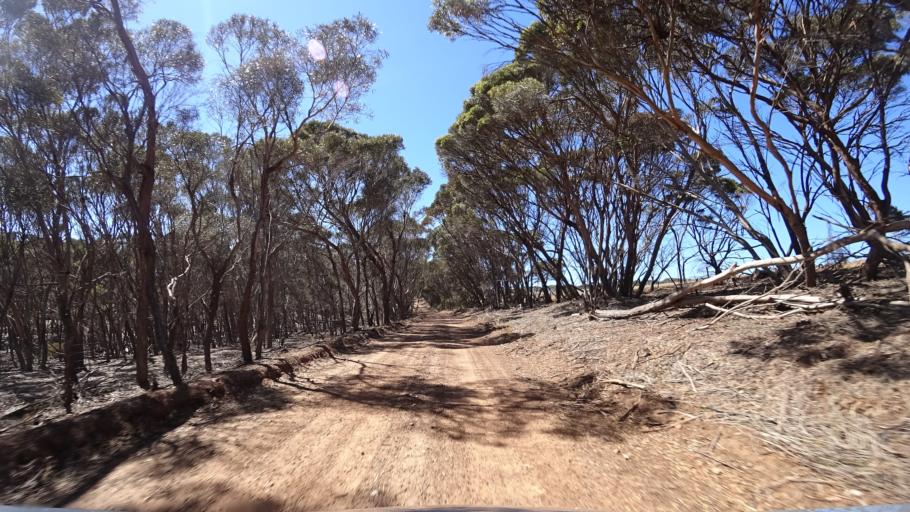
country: AU
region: South Australia
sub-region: Kangaroo Island
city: Kingscote
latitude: -35.7464
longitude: 137.7241
